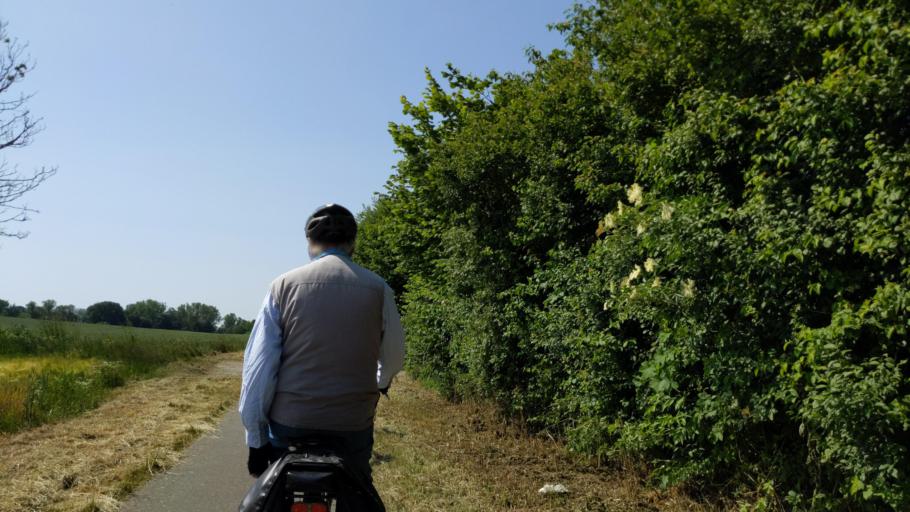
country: DE
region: Schleswig-Holstein
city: Berkenthin
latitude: 53.7451
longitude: 10.6553
